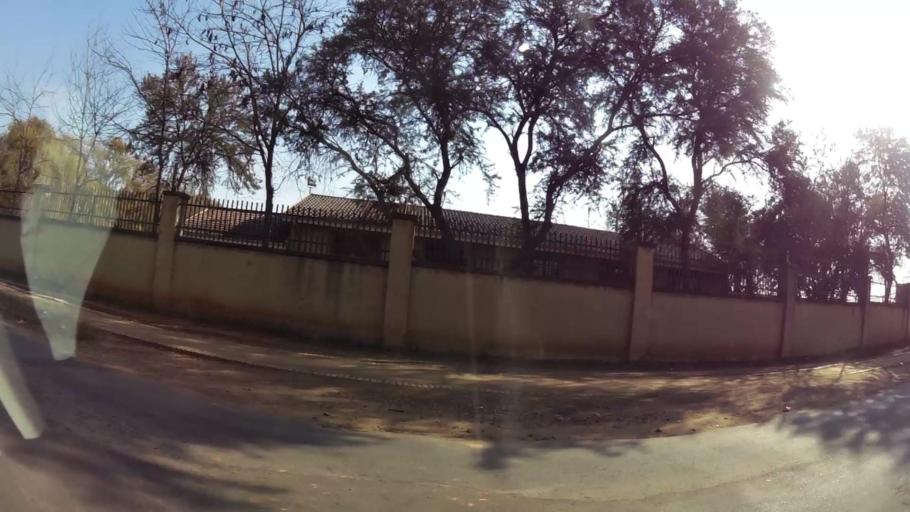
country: ZA
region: Gauteng
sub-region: City of Tshwane Metropolitan Municipality
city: Pretoria
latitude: -25.7603
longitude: 28.3390
